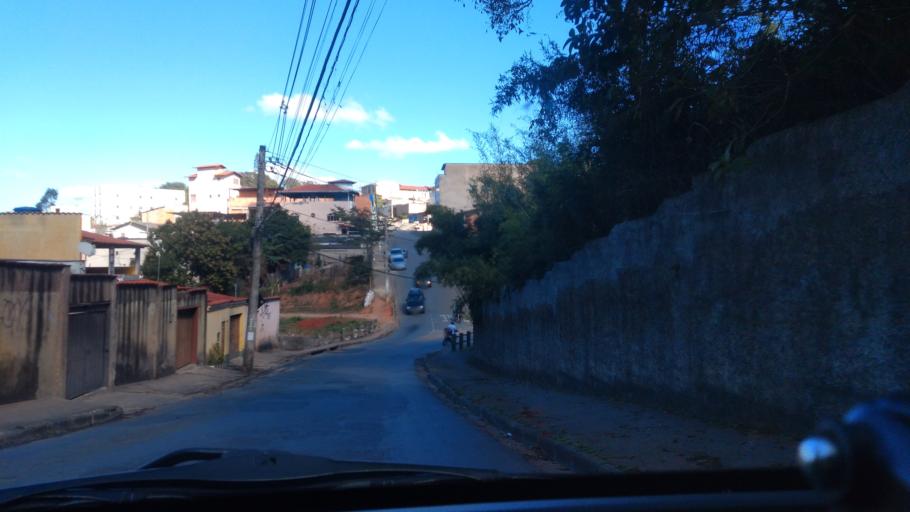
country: BR
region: Minas Gerais
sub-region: Santa Luzia
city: Santa Luzia
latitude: -19.8125
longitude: -43.9457
